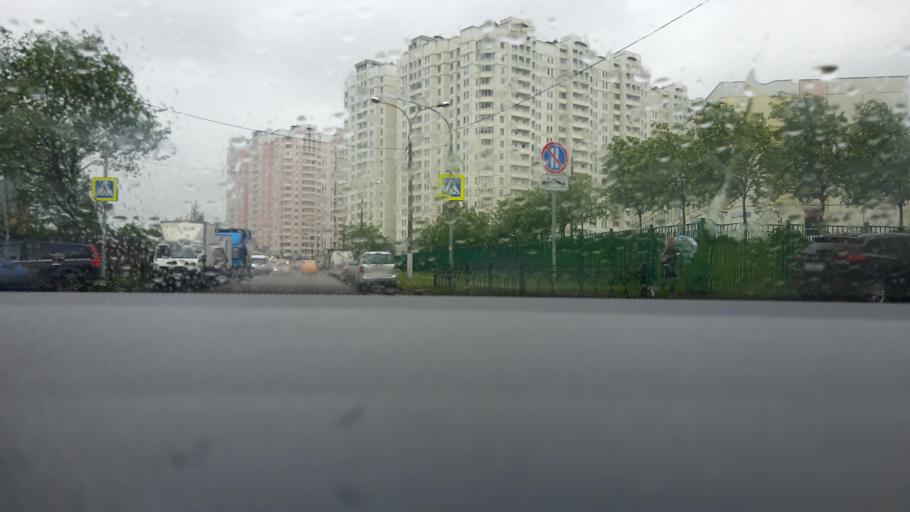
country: RU
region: Moskovskaya
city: Dubrovitsy
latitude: 55.4222
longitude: 37.4990
